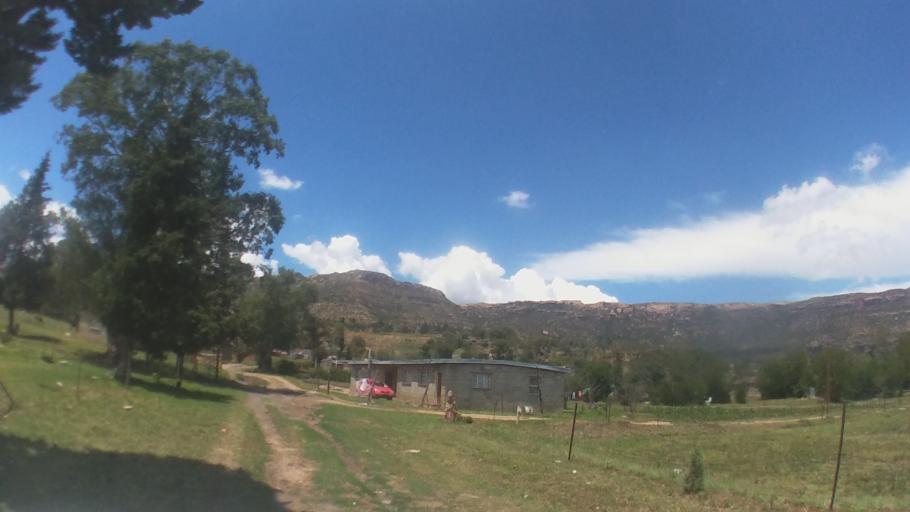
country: LS
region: Maseru
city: Nako
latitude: -29.6194
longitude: 27.5096
